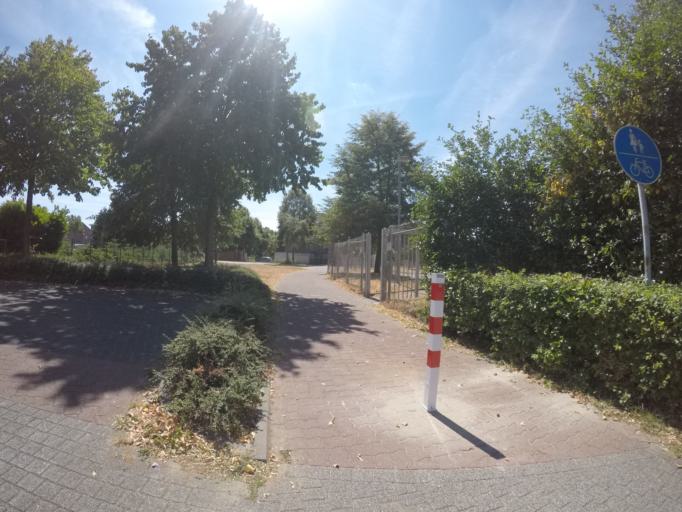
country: DE
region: North Rhine-Westphalia
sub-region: Regierungsbezirk Dusseldorf
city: Bocholt
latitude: 51.8270
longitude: 6.6103
